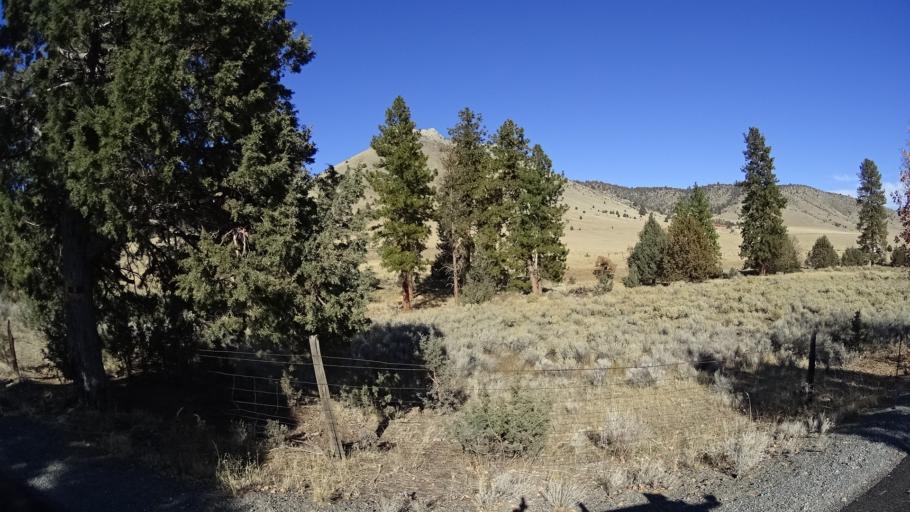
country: US
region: California
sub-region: Siskiyou County
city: Weed
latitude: 41.5039
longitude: -122.5732
